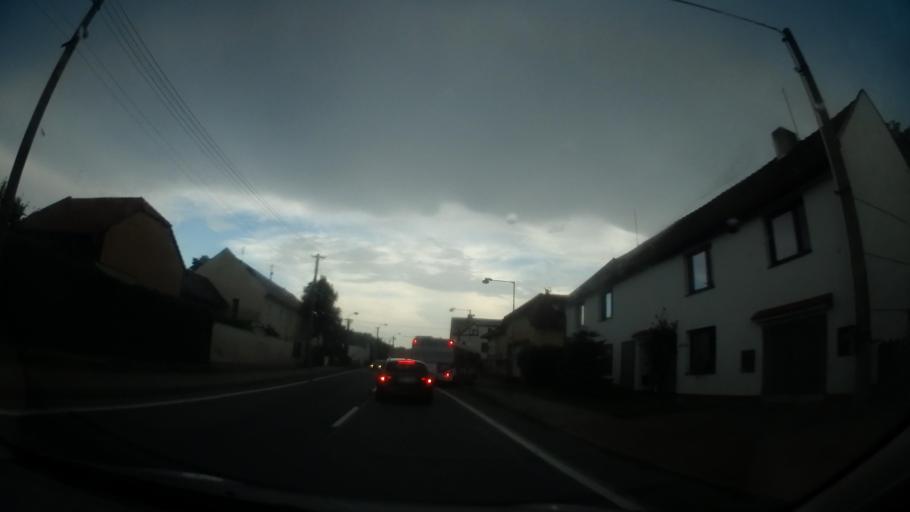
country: CZ
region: Olomoucky
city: Horka nad Moravou
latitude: 49.6405
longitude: 17.2312
